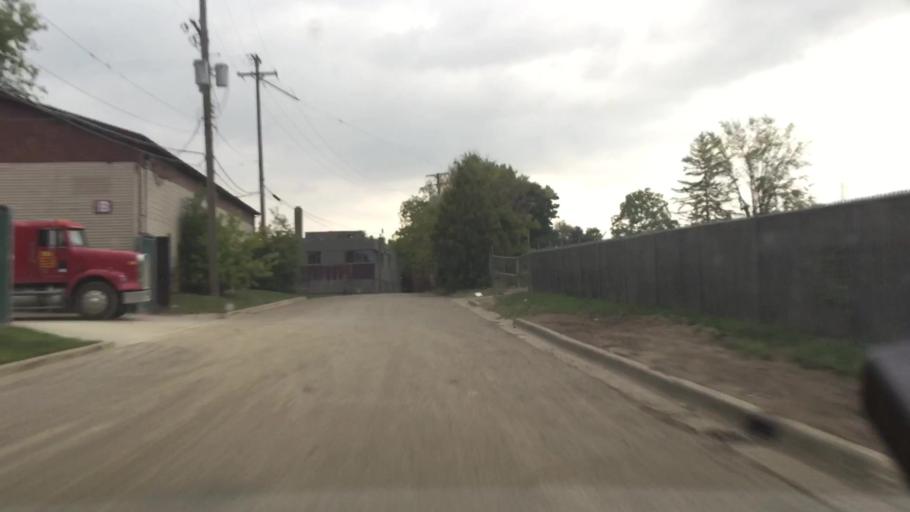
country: US
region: Michigan
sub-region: Oakland County
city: Pontiac
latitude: 42.6276
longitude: -83.2843
